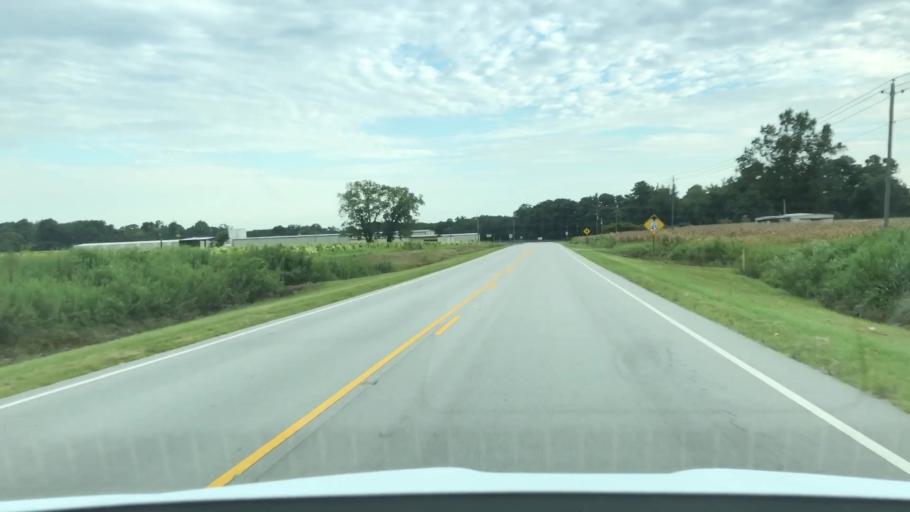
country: US
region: North Carolina
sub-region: Jones County
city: Trenton
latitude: 35.0531
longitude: -77.3559
